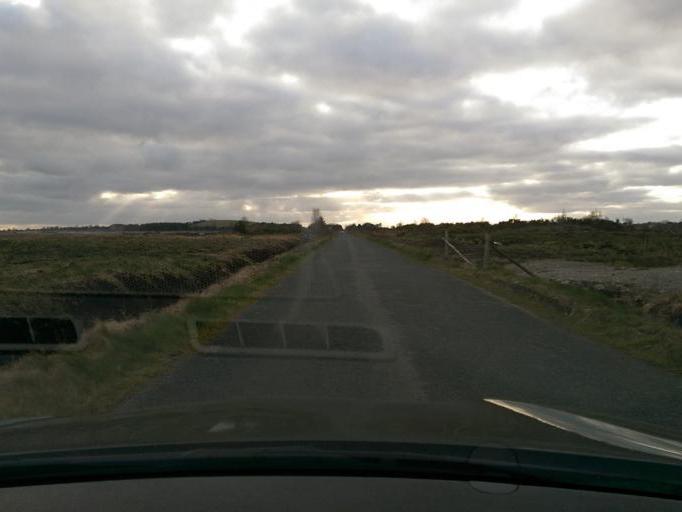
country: IE
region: Leinster
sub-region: Uibh Fhaili
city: Ferbane
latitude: 53.3290
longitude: -7.8652
